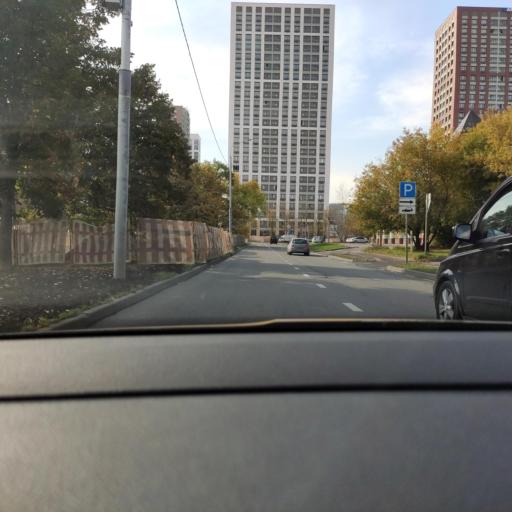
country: RU
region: Moscow
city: Metrogorodok
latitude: 55.8188
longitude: 37.7559
